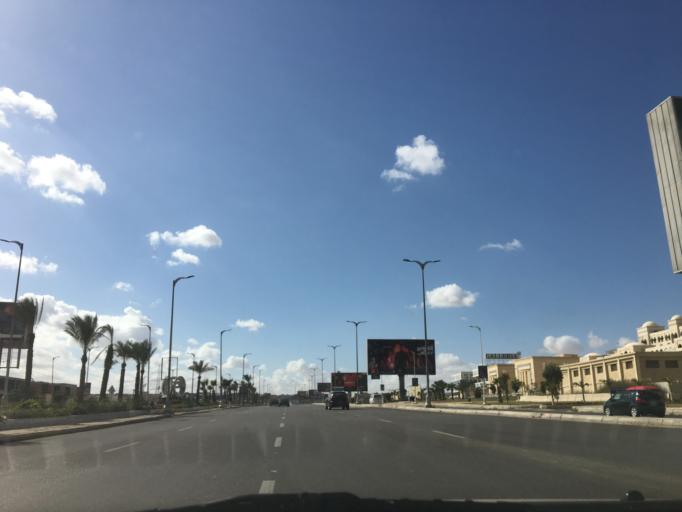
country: EG
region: Al Jizah
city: Awsim
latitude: 30.0176
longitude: 31.0053
